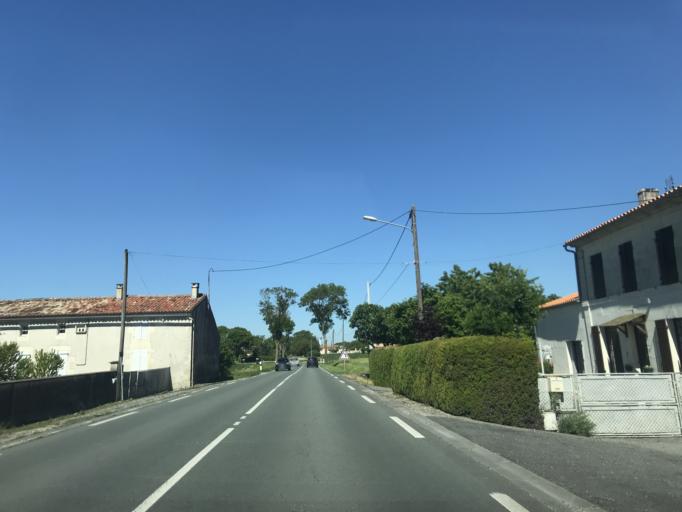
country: FR
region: Poitou-Charentes
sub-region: Departement de la Charente-Maritime
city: Perignac
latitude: 45.5776
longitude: -0.4401
